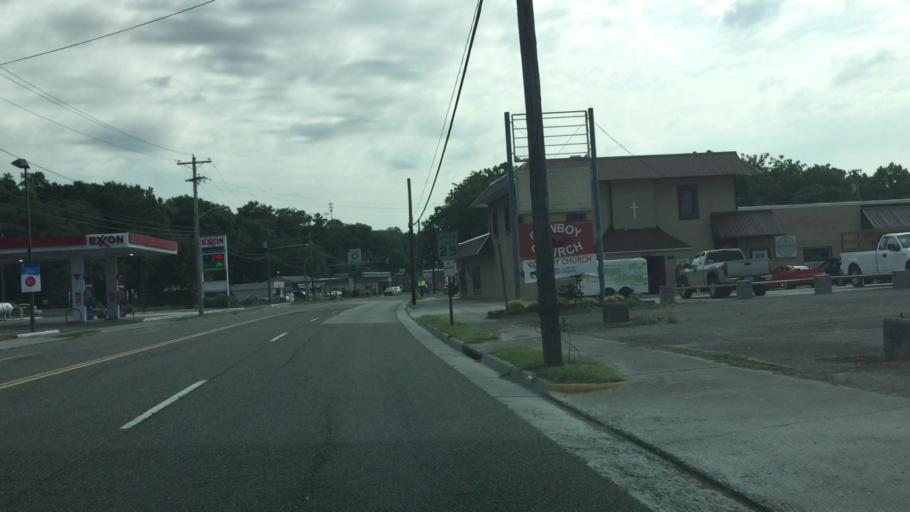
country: US
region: Virginia
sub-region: Pulaski County
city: Pulaski
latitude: 37.0482
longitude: -80.7725
